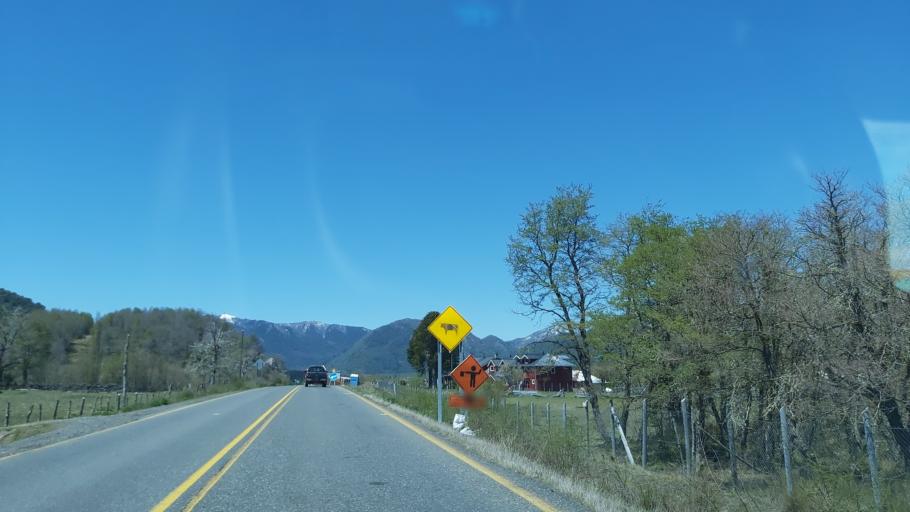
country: CL
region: Araucania
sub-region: Provincia de Cautin
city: Vilcun
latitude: -38.4654
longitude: -71.6061
